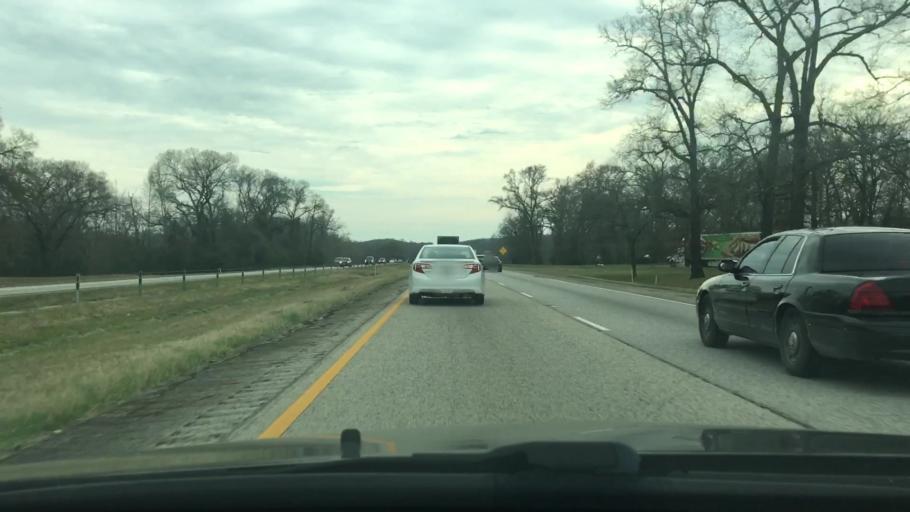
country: US
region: Texas
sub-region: Leon County
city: Centerville
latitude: 31.1948
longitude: -95.9934
